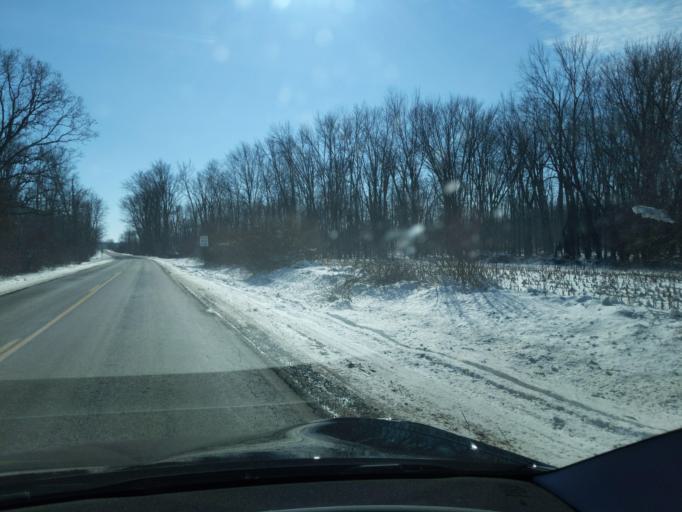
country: US
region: Michigan
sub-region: Ingham County
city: Stockbridge
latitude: 42.5121
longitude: -84.0730
